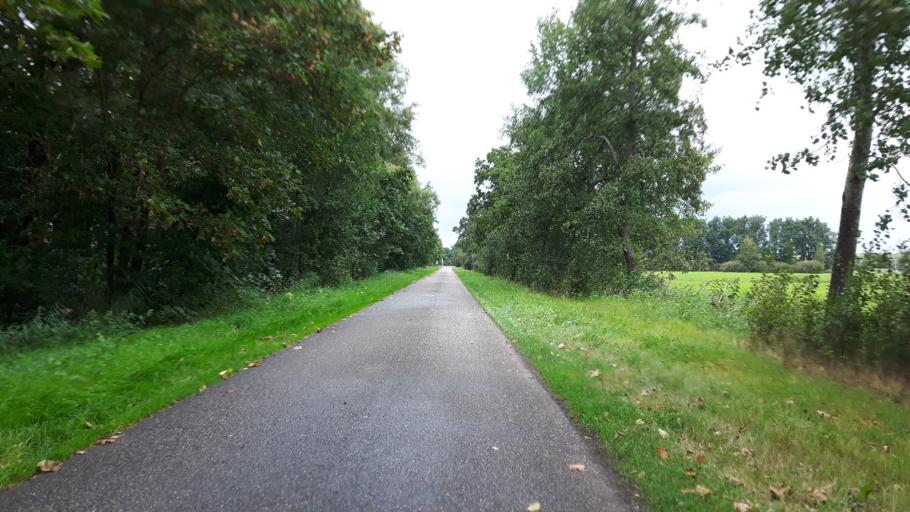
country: NL
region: Friesland
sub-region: Gemeente Dantumadiel
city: Broeksterwald
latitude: 53.2684
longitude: 5.9839
